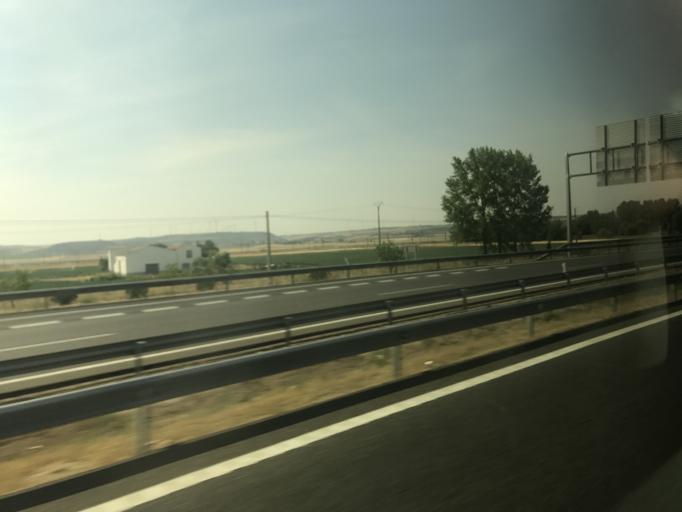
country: ES
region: Castille and Leon
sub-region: Provincia de Palencia
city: Quintana del Puente
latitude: 42.0749
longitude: -4.2131
